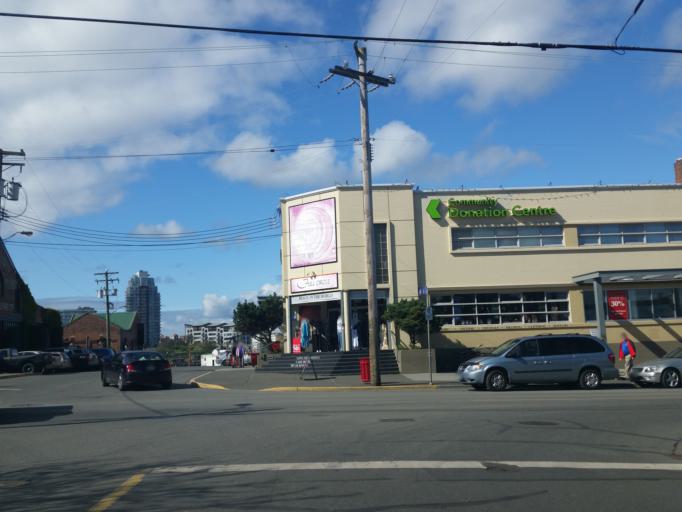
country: CA
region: British Columbia
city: Victoria
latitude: 48.4302
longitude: -123.3694
